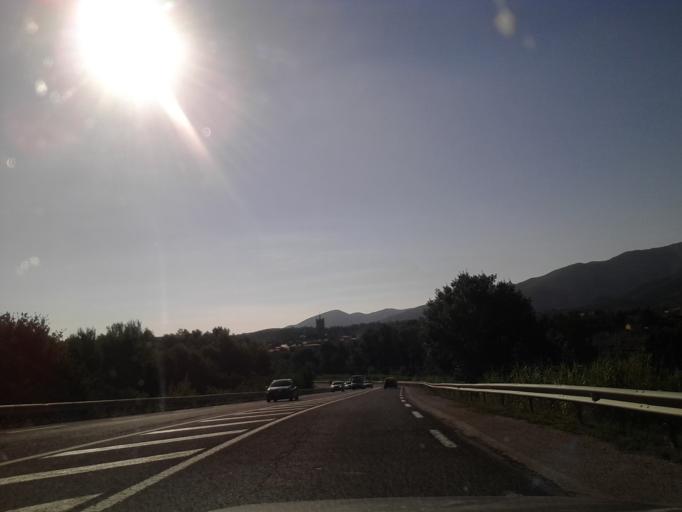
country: FR
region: Languedoc-Roussillon
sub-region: Departement des Pyrenees-Orientales
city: Vinca
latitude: 42.6470
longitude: 2.5189
